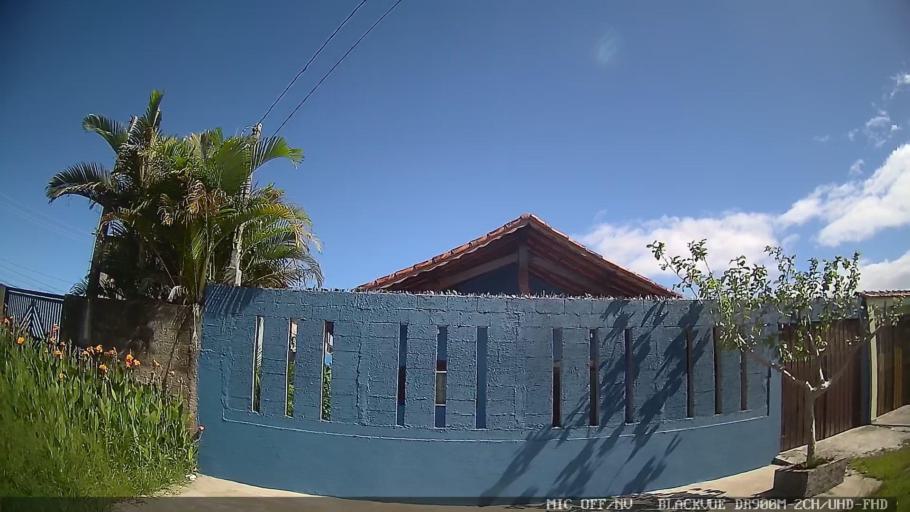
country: BR
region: Sao Paulo
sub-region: Itanhaem
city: Itanhaem
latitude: -24.2247
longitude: -46.8762
